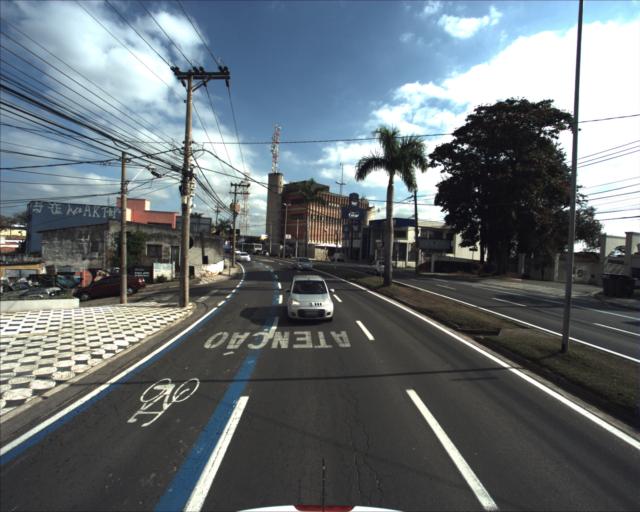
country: BR
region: Sao Paulo
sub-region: Sorocaba
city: Sorocaba
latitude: -23.5103
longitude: -47.4882
